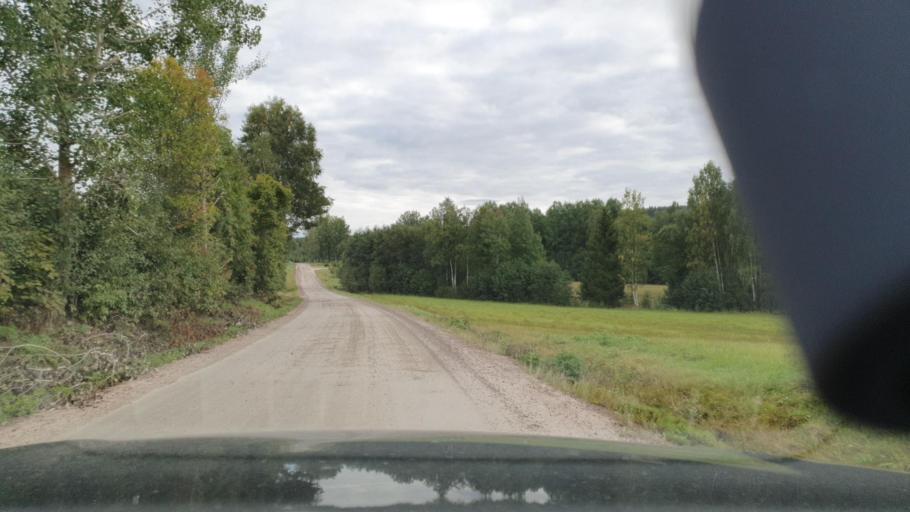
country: SE
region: Vaermland
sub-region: Hagfors Kommun
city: Ekshaerad
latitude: 60.0126
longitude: 13.4679
